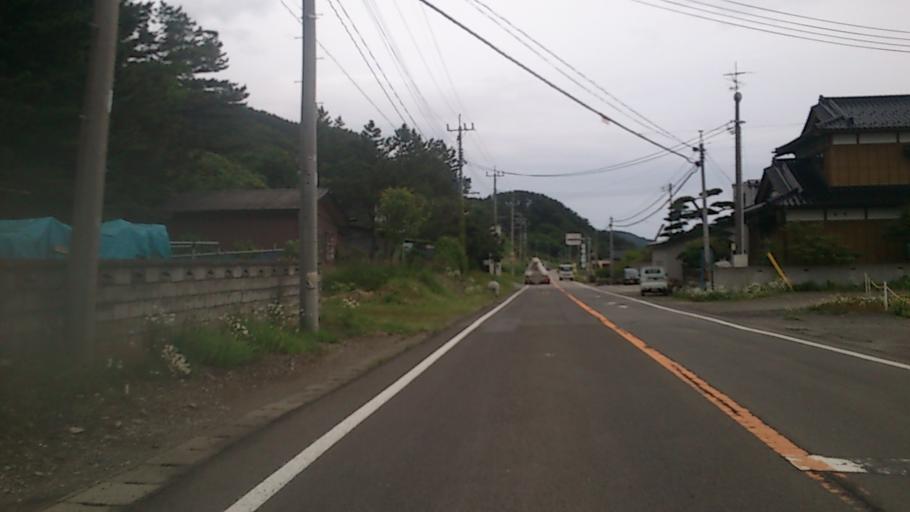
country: JP
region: Akita
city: Noshiromachi
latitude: 40.5110
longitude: 139.9507
